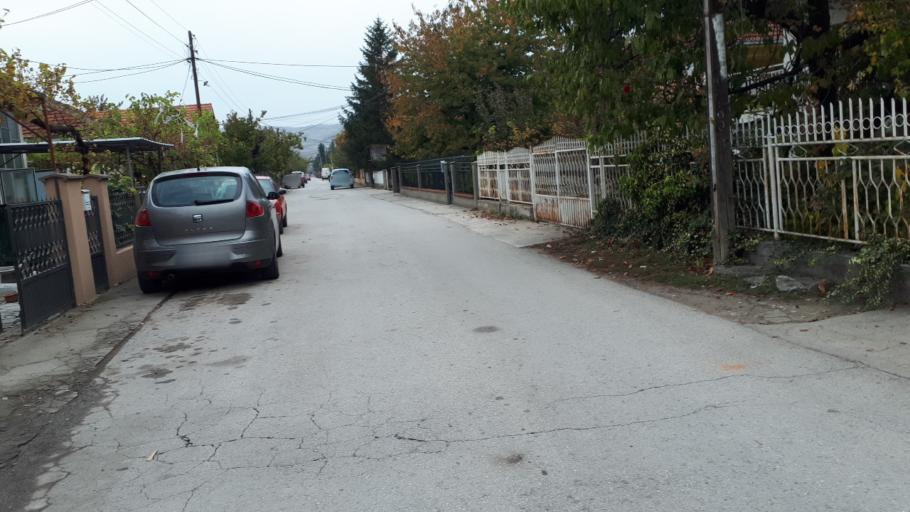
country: MK
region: Saraj
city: Saraj
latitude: 42.0208
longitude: 21.3571
